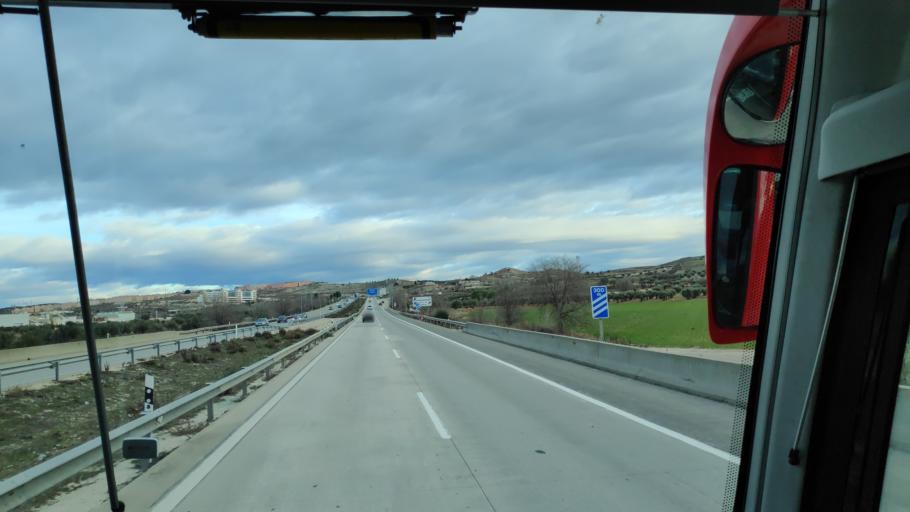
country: ES
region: Madrid
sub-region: Provincia de Madrid
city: Arganda
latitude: 40.2978
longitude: -3.4774
